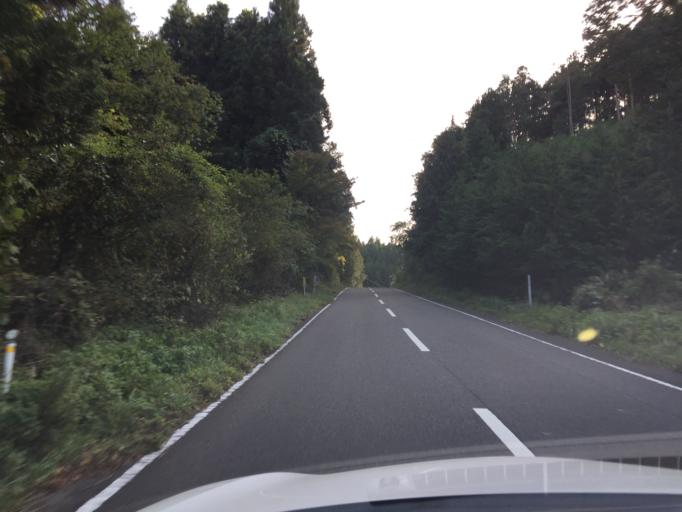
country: JP
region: Fukushima
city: Ishikawa
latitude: 37.2123
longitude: 140.5981
